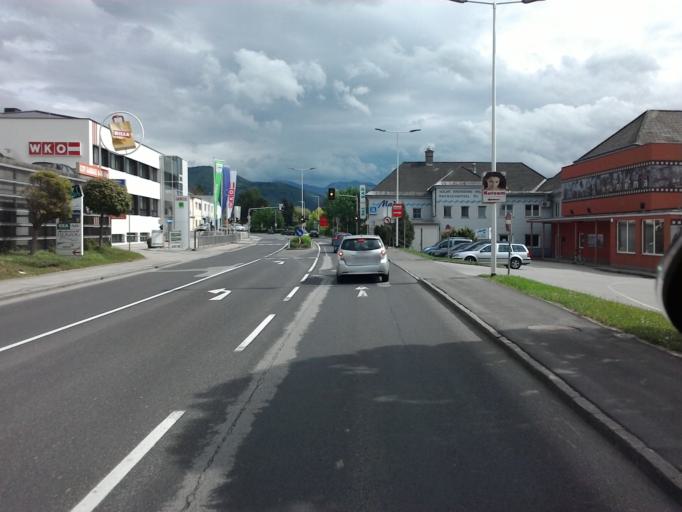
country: AT
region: Upper Austria
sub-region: Politischer Bezirk Kirchdorf an der Krems
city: Micheldorf in Oberoesterreich
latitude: 47.9059
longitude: 14.1198
